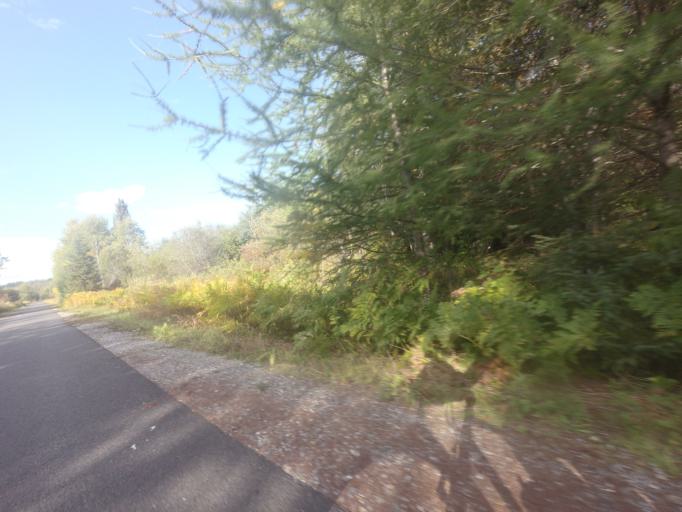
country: CA
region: Quebec
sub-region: Laurentides
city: Labelle
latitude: 46.3070
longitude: -74.7663
